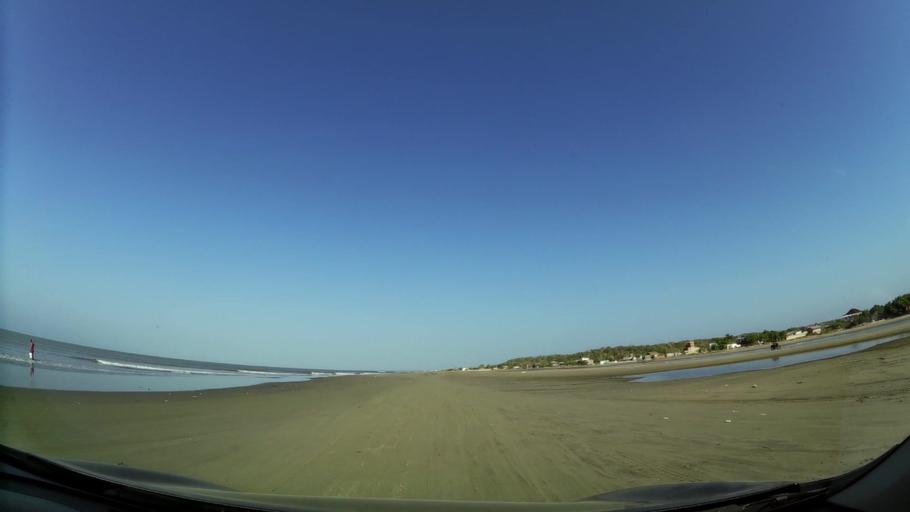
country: CO
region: Bolivar
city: Cartagena
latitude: 10.4924
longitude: -75.4949
